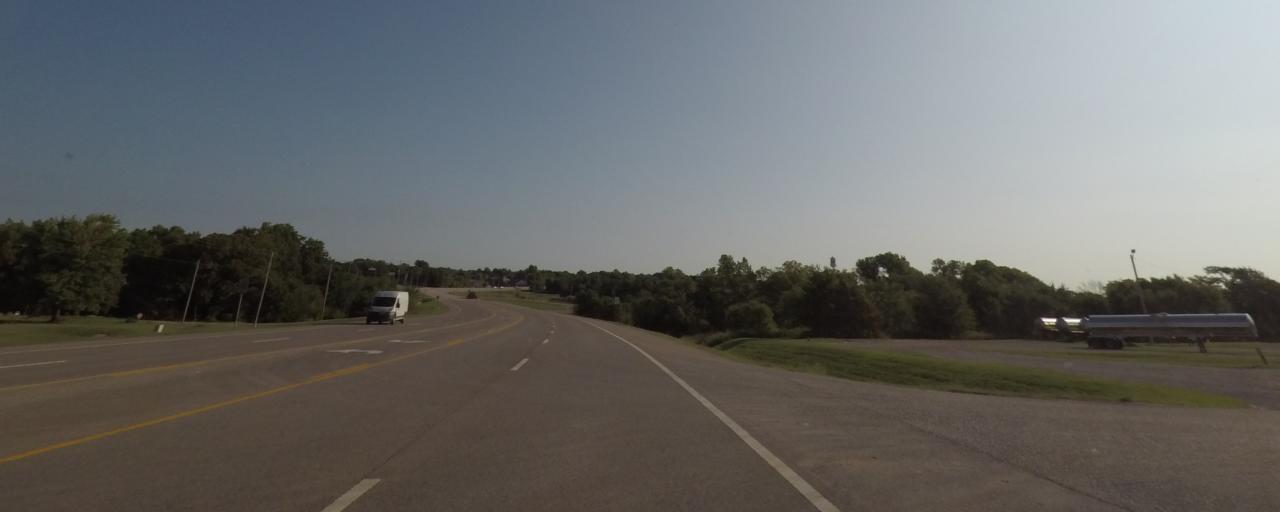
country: US
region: Oklahoma
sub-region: McClain County
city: Blanchard
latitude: 35.1321
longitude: -97.6658
